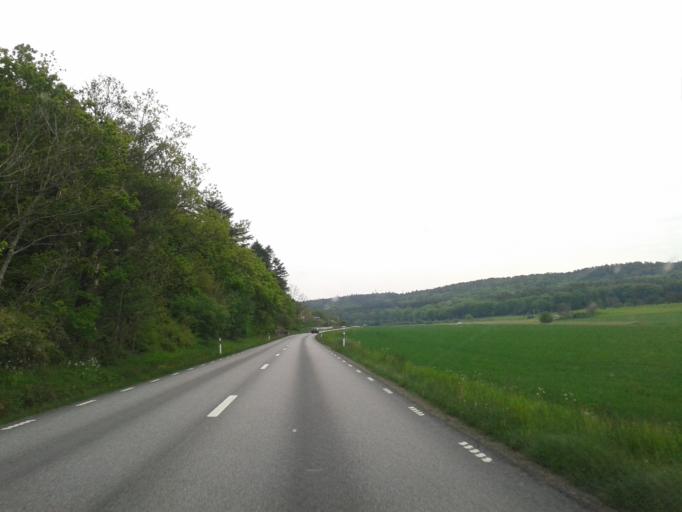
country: SE
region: Vaestra Goetaland
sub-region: Kungalvs Kommun
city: Kode
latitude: 57.8912
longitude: 11.7651
